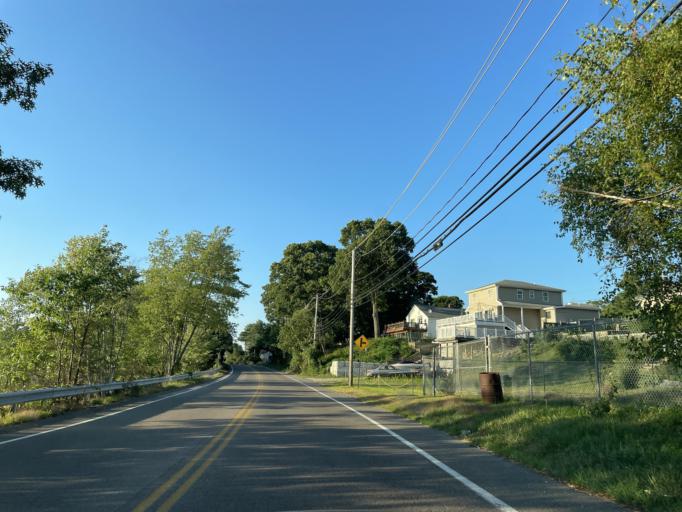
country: US
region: Massachusetts
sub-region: Plymouth County
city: Halifax
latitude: 42.0029
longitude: -70.8415
